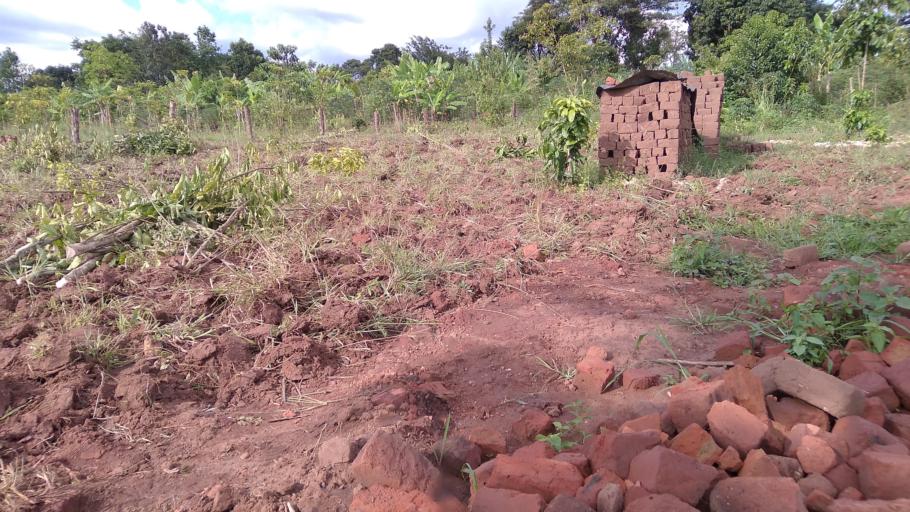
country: UG
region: Central Region
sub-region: Wakiso District
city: Wakiso
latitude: 0.5069
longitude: 32.5606
